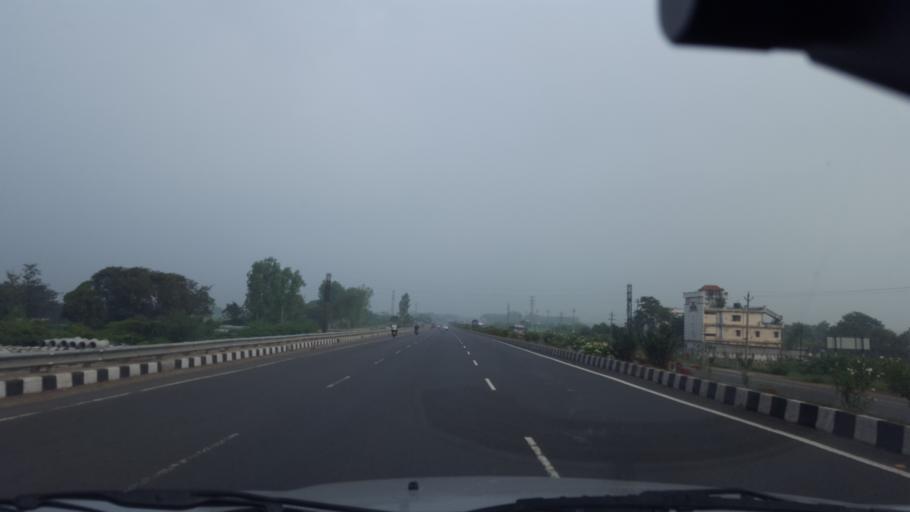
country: IN
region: Andhra Pradesh
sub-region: Prakasam
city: Ongole
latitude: 15.6431
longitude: 80.0157
